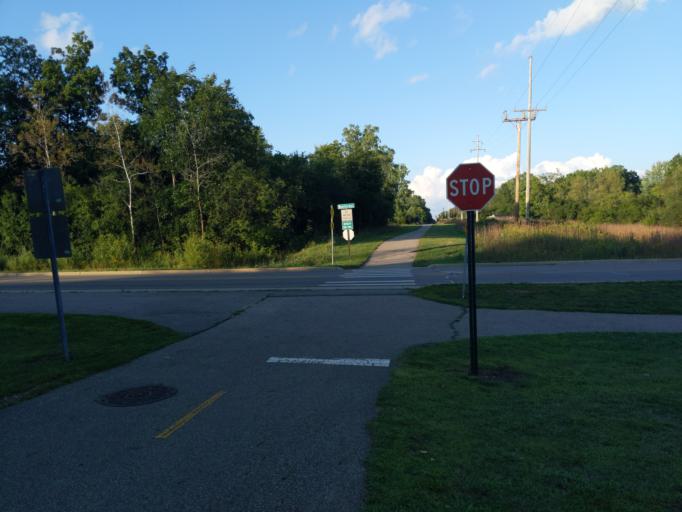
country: US
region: Michigan
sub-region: Jackson County
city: Vandercook Lake
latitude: 42.2100
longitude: -84.4418
